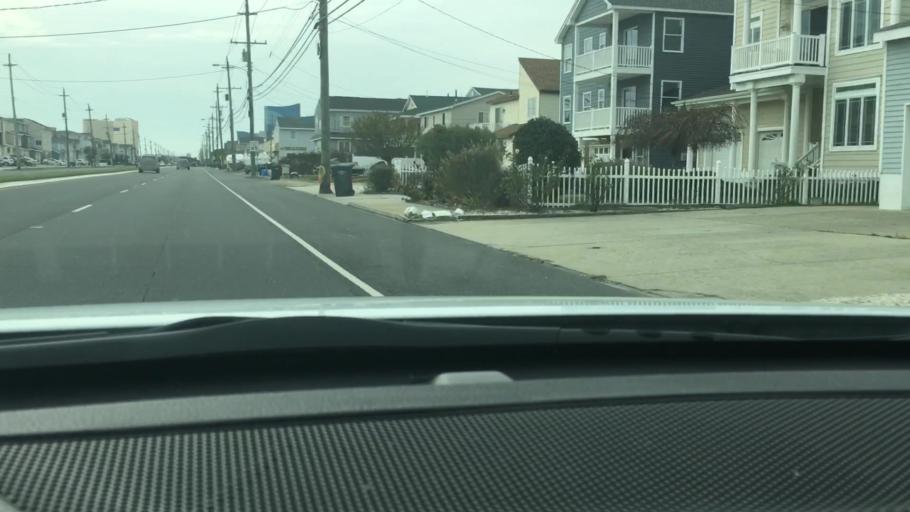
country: US
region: New Jersey
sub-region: Atlantic County
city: Atlantic City
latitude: 39.3933
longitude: -74.4056
